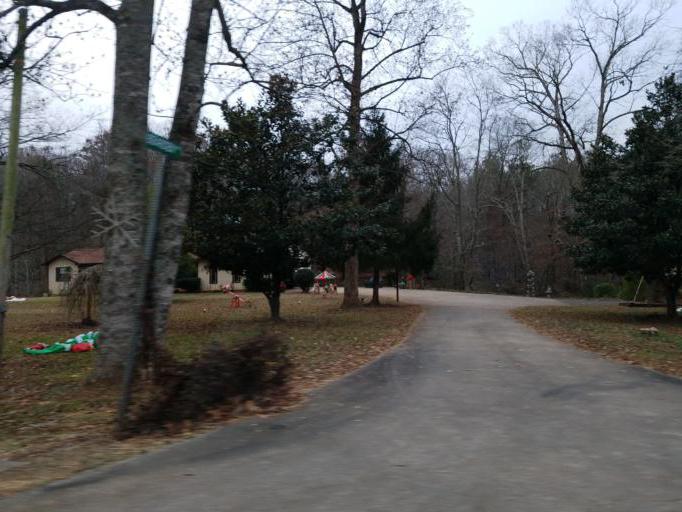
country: US
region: Georgia
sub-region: Dawson County
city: Dawsonville
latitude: 34.4442
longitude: -84.1016
